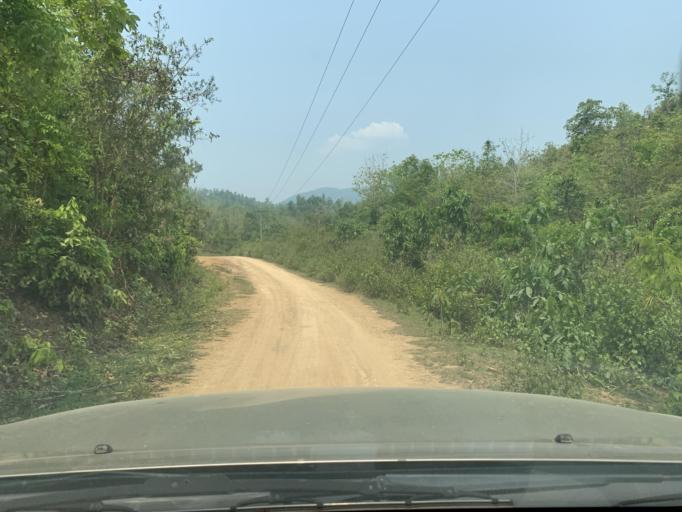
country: LA
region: Louangphabang
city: Louangphabang
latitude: 19.9517
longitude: 102.1290
